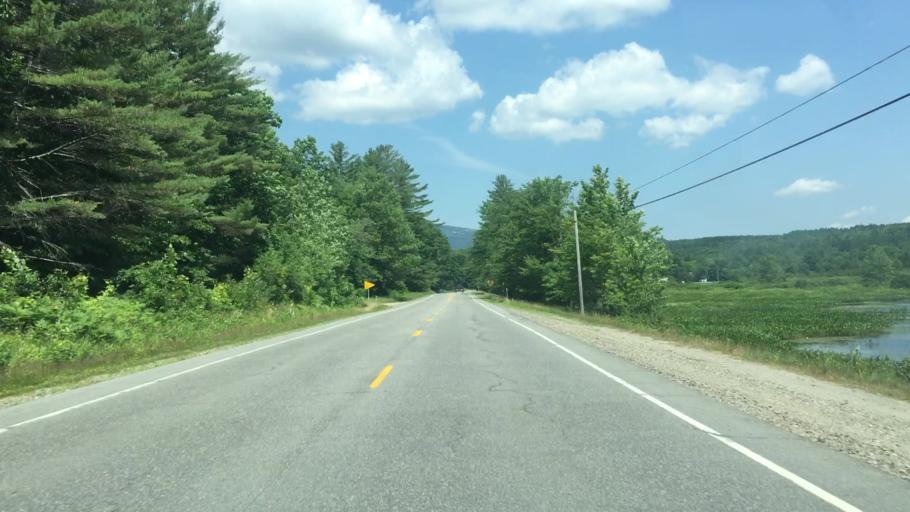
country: US
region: New Hampshire
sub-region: Sullivan County
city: Grantham
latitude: 43.4448
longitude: -72.1589
